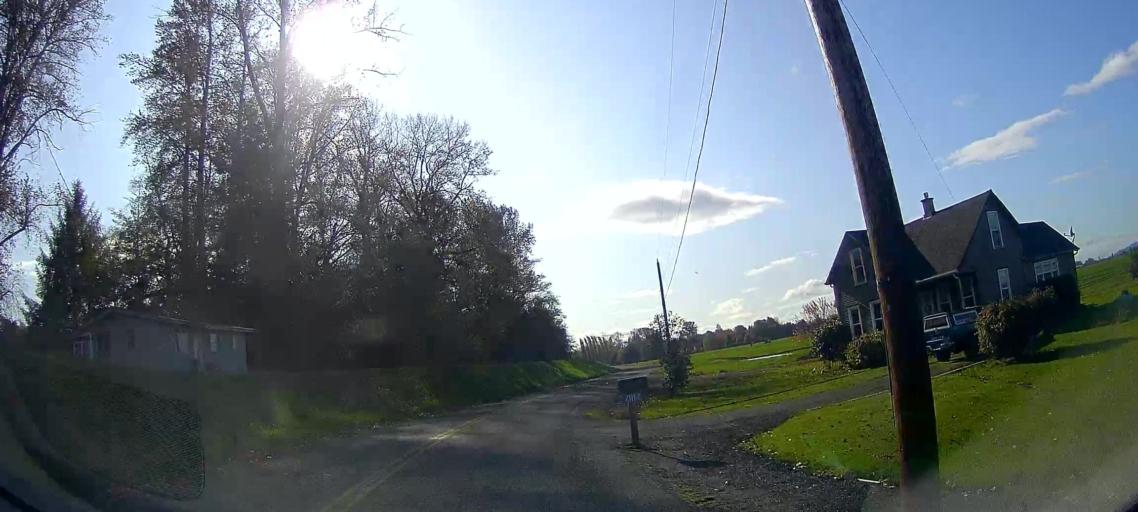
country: US
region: Washington
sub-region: Skagit County
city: Mount Vernon
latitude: 48.3349
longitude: -122.3510
